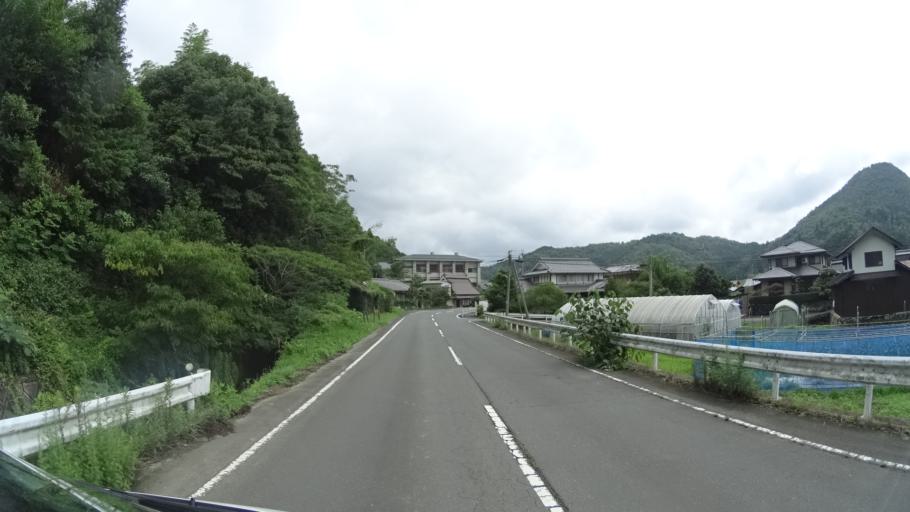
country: JP
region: Kyoto
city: Kameoka
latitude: 35.0888
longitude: 135.4397
